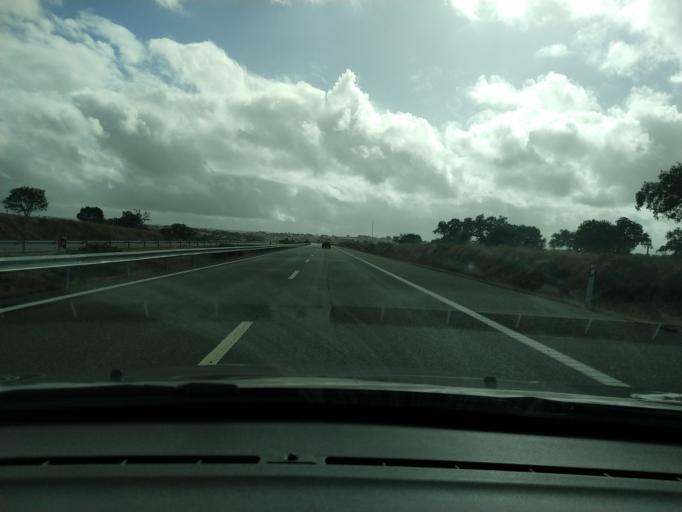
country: PT
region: Beja
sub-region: Ourique
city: Ourique
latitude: 37.5804
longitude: -8.1856
